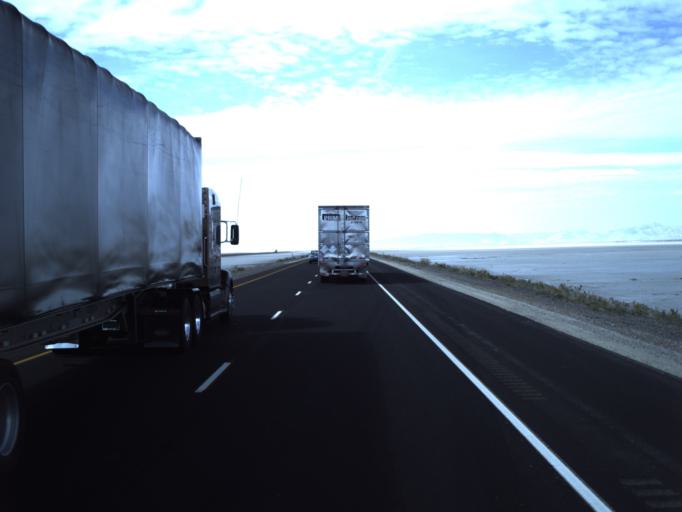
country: US
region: Utah
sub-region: Tooele County
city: Wendover
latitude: 40.7331
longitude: -113.5550
